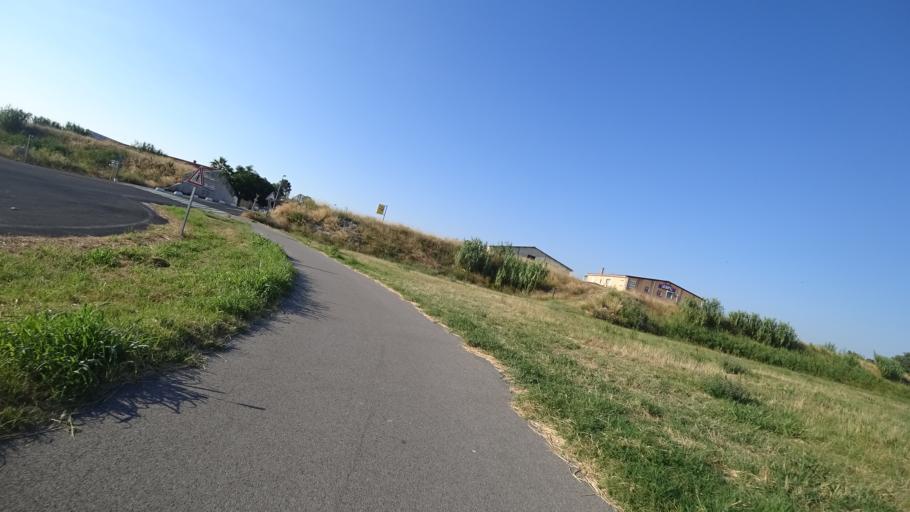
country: FR
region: Languedoc-Roussillon
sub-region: Departement des Pyrenees-Orientales
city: Canet-en-Roussillon
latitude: 42.7087
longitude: 3.0188
